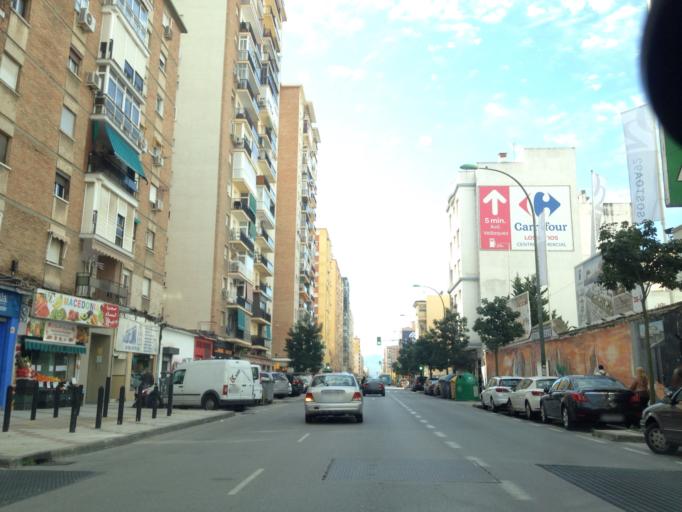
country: ES
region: Andalusia
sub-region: Provincia de Malaga
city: Malaga
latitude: 36.7072
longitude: -4.4362
